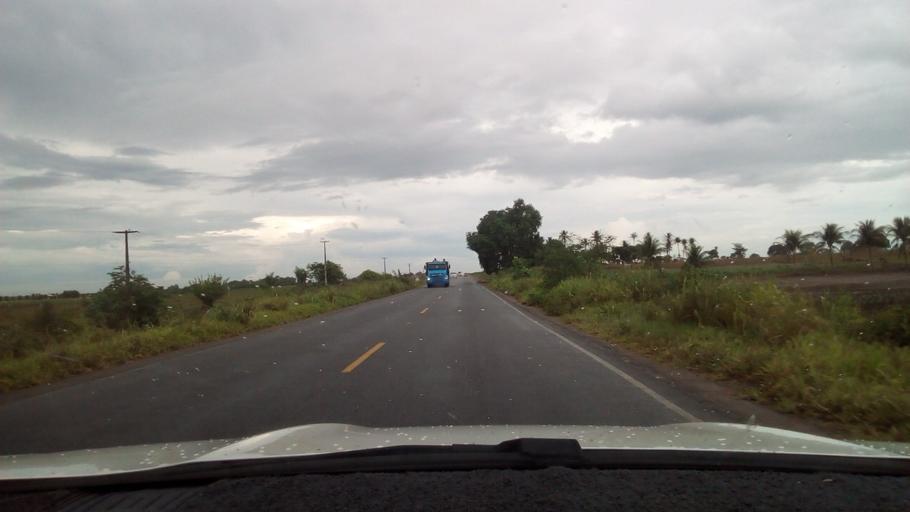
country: BR
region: Paraiba
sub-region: Mari
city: Mari
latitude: -7.0646
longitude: -35.2909
